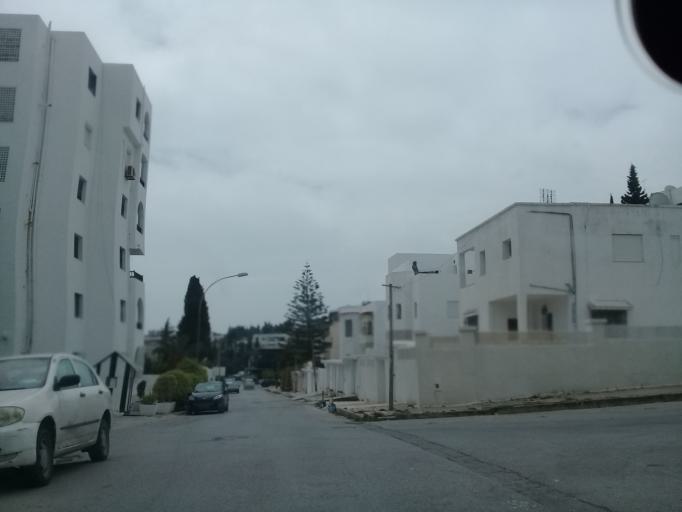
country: TN
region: Tunis
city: Tunis
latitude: 36.8361
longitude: 10.1560
